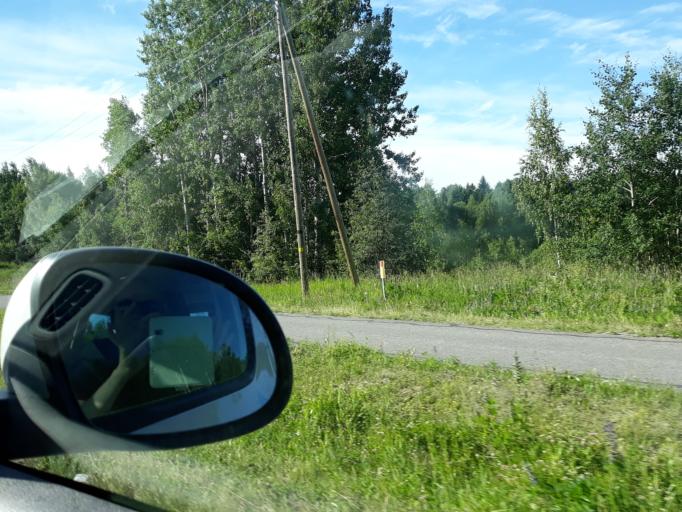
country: FI
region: Uusimaa
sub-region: Helsinki
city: Jaervenpaeae
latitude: 60.5461
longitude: 24.9840
